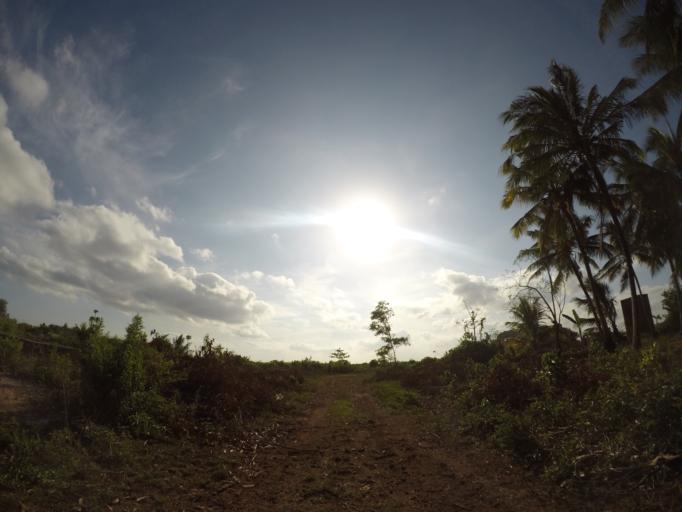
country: TZ
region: Zanzibar Central/South
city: Koani
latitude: -6.2064
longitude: 39.3156
